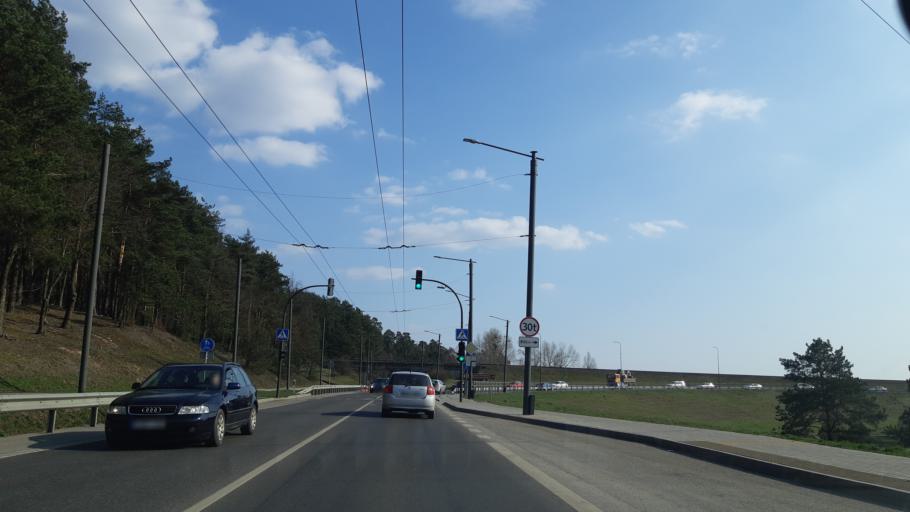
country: LT
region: Kauno apskritis
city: Dainava (Kaunas)
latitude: 54.8808
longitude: 24.0104
